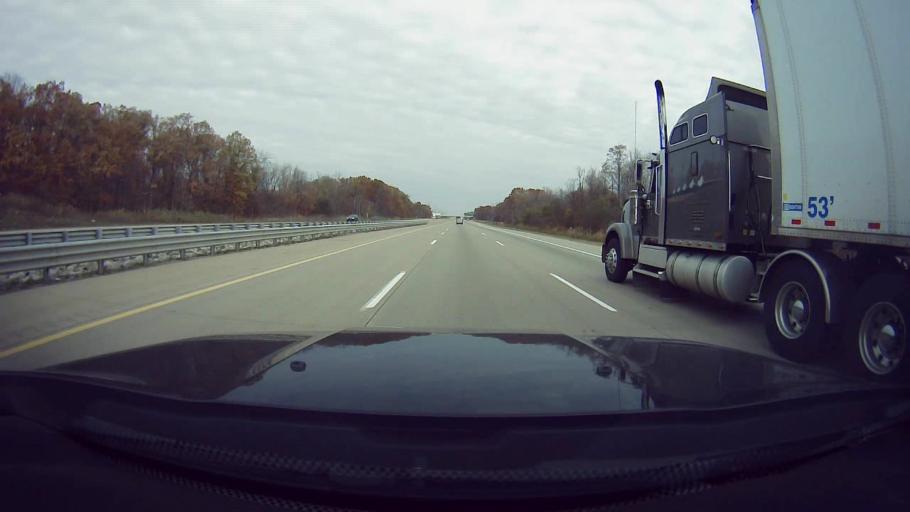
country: US
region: Michigan
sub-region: Wayne County
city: Rockwood
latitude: 42.0875
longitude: -83.2417
